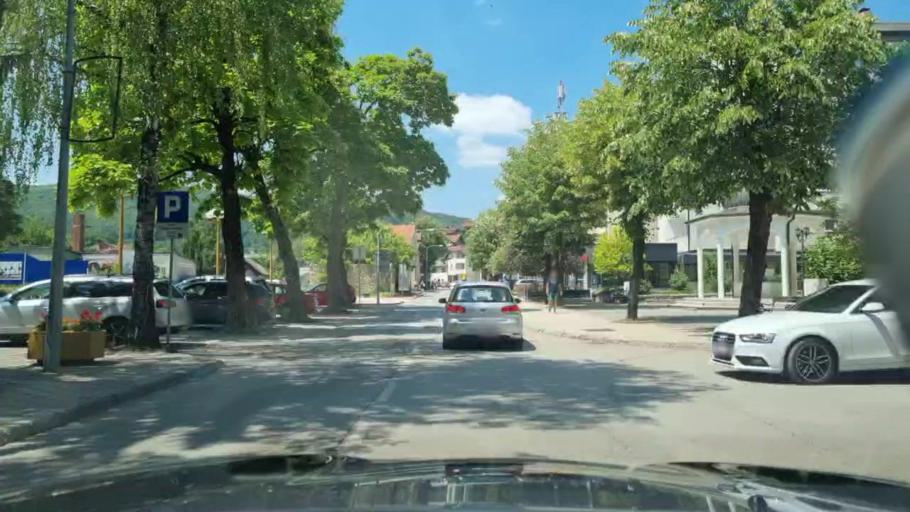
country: BA
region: Federation of Bosnia and Herzegovina
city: Kljuc
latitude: 44.5330
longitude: 16.7747
